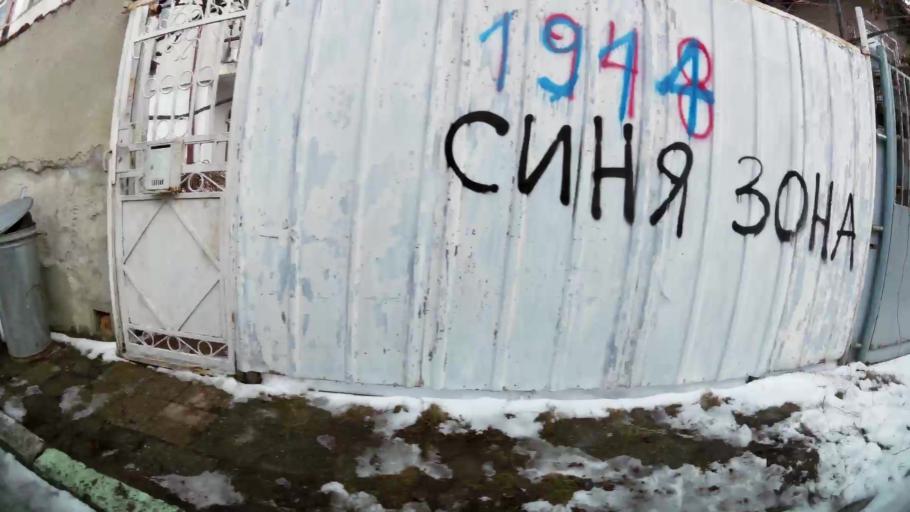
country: BG
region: Sofia-Capital
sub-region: Stolichna Obshtina
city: Sofia
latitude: 42.7008
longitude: 23.3800
